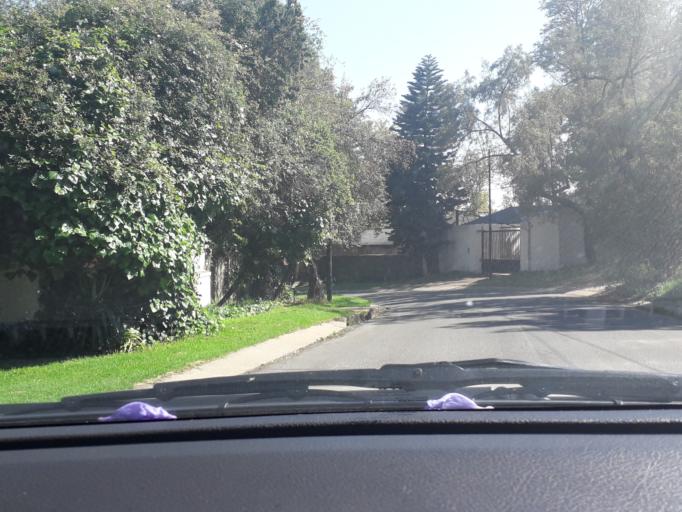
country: ZA
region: Gauteng
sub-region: City of Johannesburg Metropolitan Municipality
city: Johannesburg
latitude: -26.1153
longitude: 28.0739
